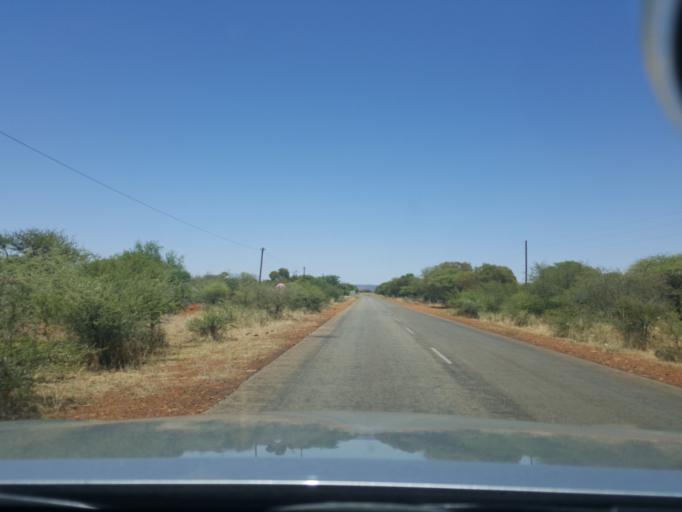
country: BW
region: South East
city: Otse
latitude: -25.1118
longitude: 25.9527
